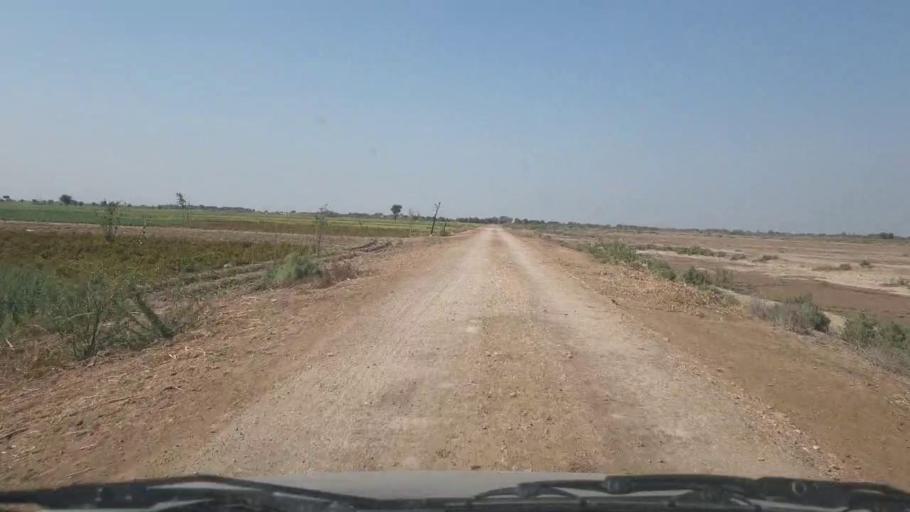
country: PK
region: Sindh
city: Samaro
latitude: 25.2335
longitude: 69.3367
